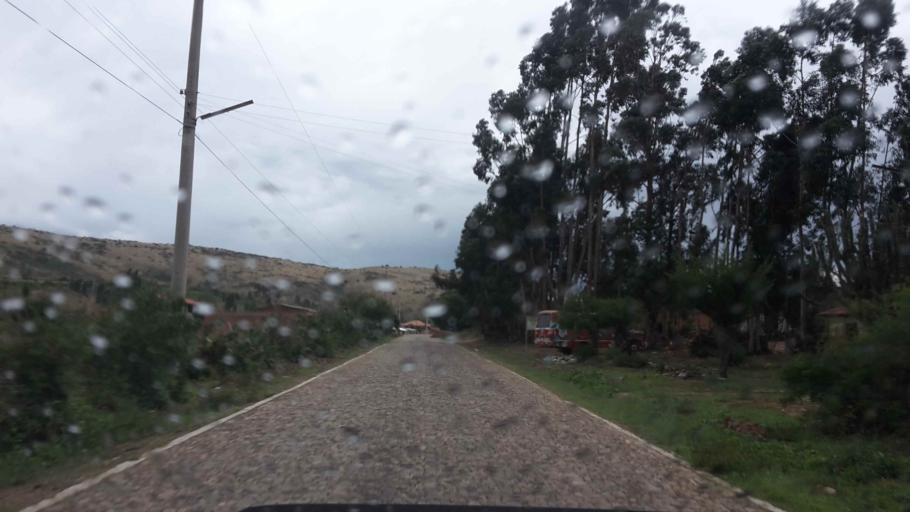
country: BO
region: Cochabamba
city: Cochabamba
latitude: -17.5497
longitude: -66.1735
